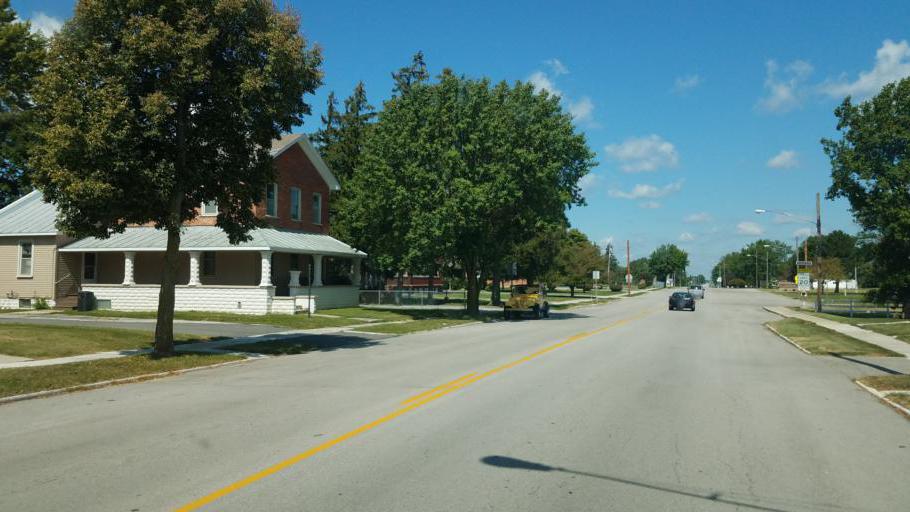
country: US
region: Ohio
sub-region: Wyandot County
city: Carey
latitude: 41.0535
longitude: -83.3200
